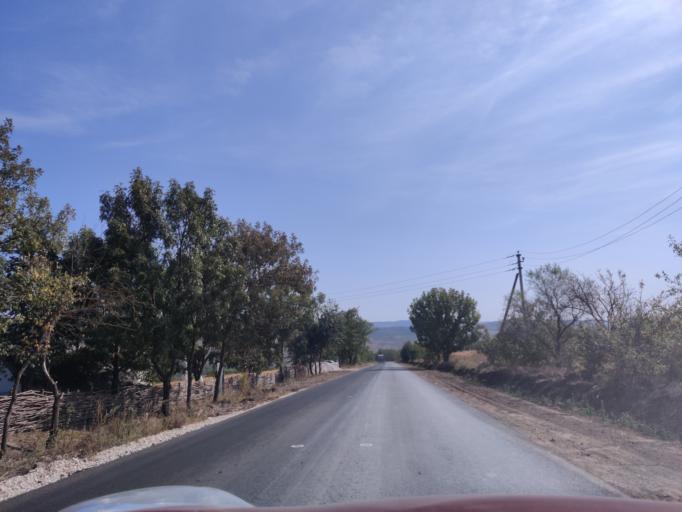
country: MD
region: Ungheni
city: Ungheni
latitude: 47.2626
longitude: 27.9810
